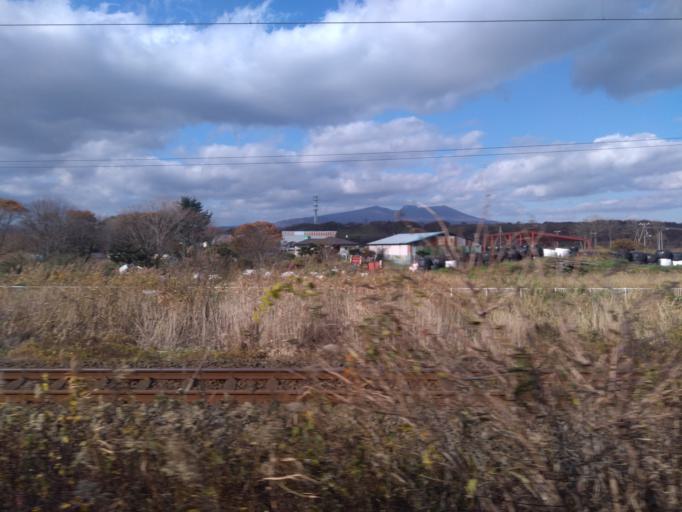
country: JP
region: Hokkaido
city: Shiraoi
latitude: 42.5808
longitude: 141.4229
